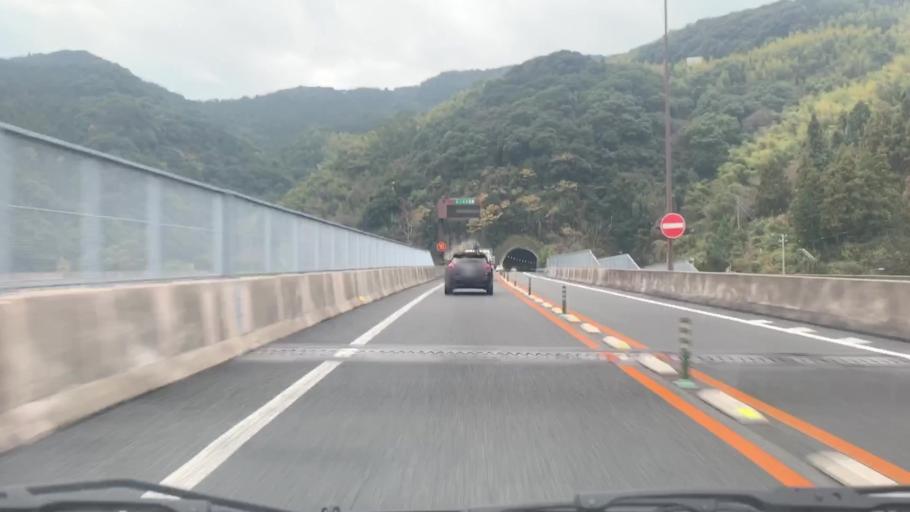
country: JP
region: Nagasaki
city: Nagasaki-shi
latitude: 32.7529
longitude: 129.9278
